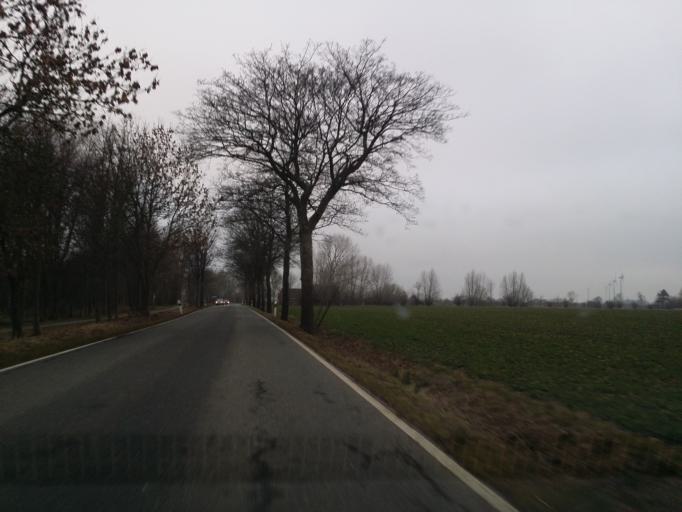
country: DE
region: Schleswig-Holstein
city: Fehmarn
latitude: 54.4615
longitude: 11.1217
